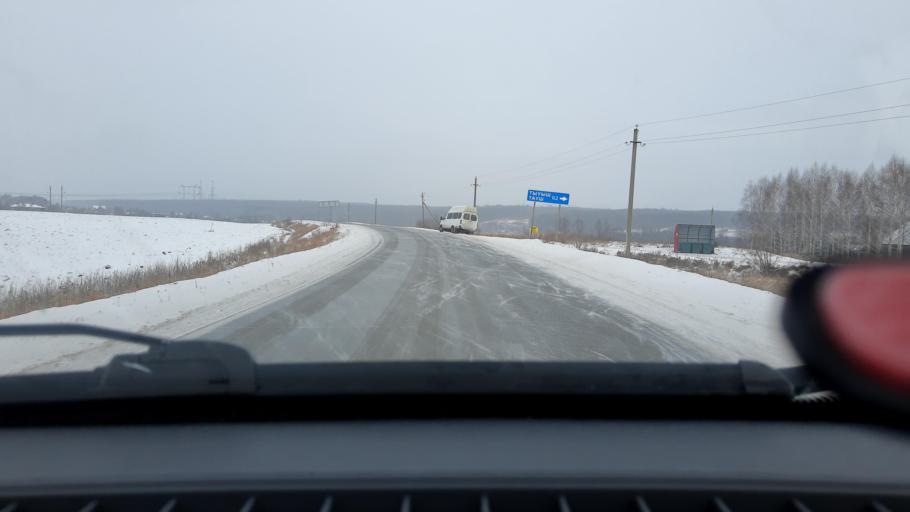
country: RU
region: Bashkortostan
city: Iglino
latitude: 54.7523
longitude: 56.4001
